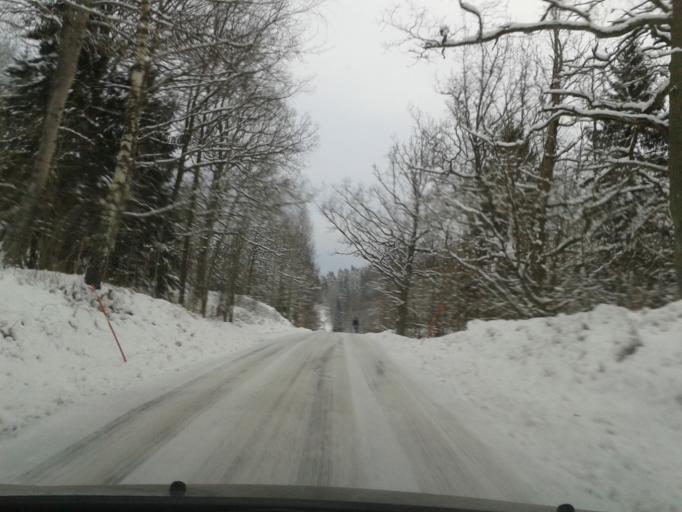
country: SE
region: Stockholm
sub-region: Tyreso Kommun
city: Brevik
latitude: 59.2106
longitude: 18.3103
